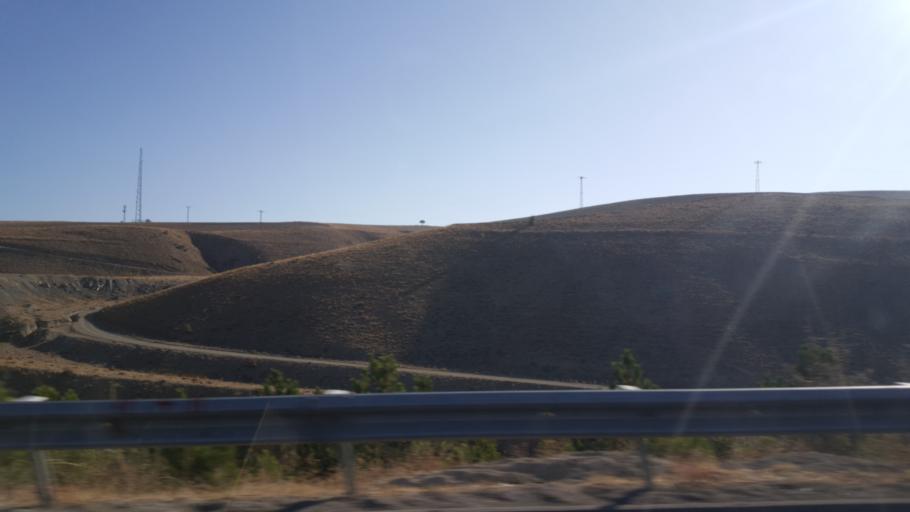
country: TR
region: Ankara
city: Cankaya
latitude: 39.8436
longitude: 32.8926
